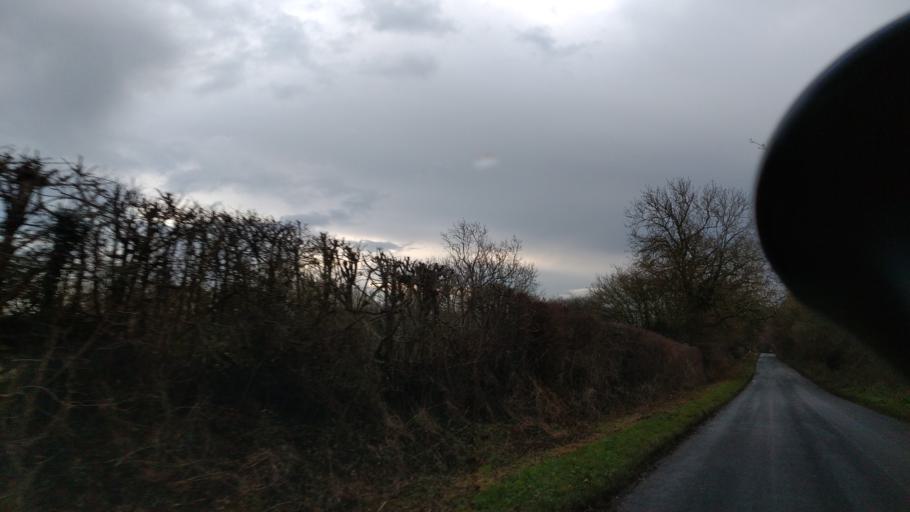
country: GB
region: England
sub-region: Borough of Swindon
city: Highworth
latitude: 51.6018
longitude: -1.7280
